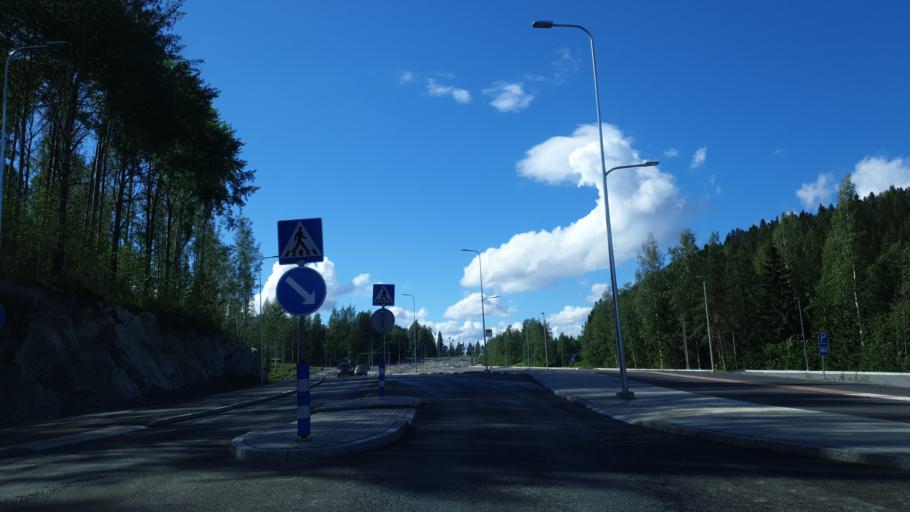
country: FI
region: Northern Savo
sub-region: Kuopio
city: Kuopio
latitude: 62.9035
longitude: 27.6589
